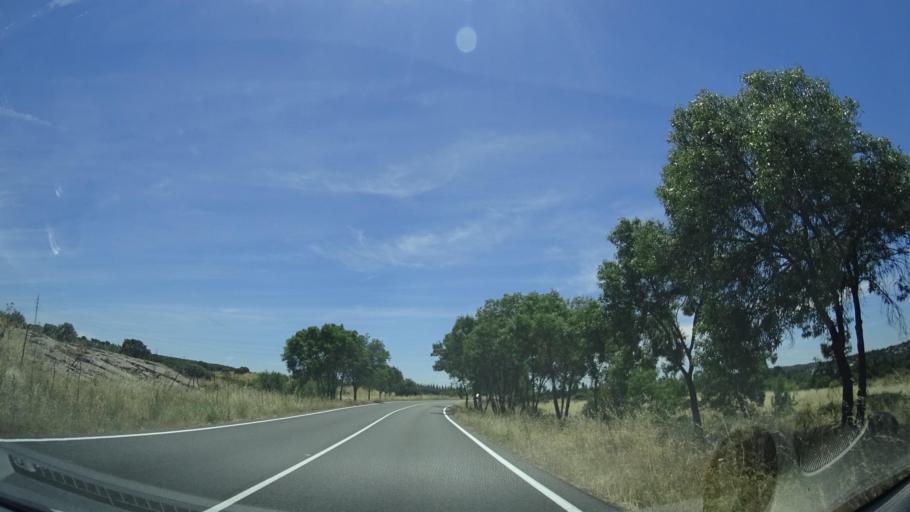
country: ES
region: Madrid
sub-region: Provincia de Madrid
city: Collado-Villalba
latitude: 40.6103
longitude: -3.9807
